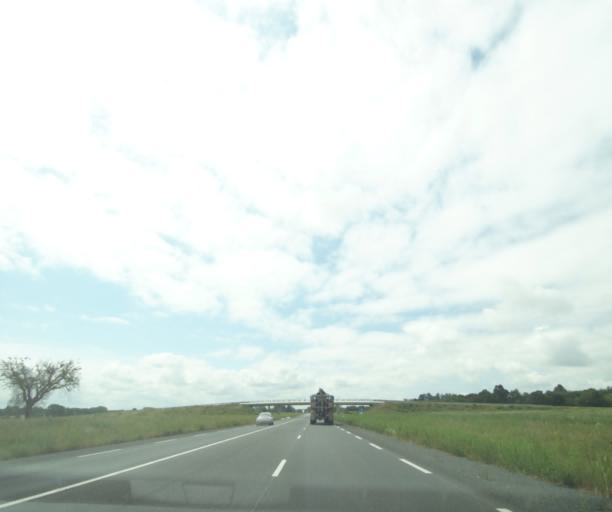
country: FR
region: Poitou-Charentes
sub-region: Departement des Deux-Sevres
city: Louzy
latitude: 47.0305
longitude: -0.2009
